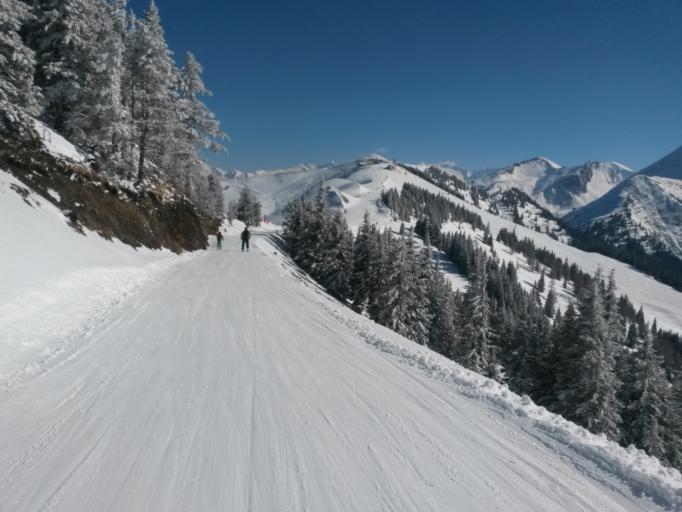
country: AT
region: Salzburg
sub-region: Politischer Bezirk Sankt Johann im Pongau
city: Dorfgastein
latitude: 47.2330
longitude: 13.1473
